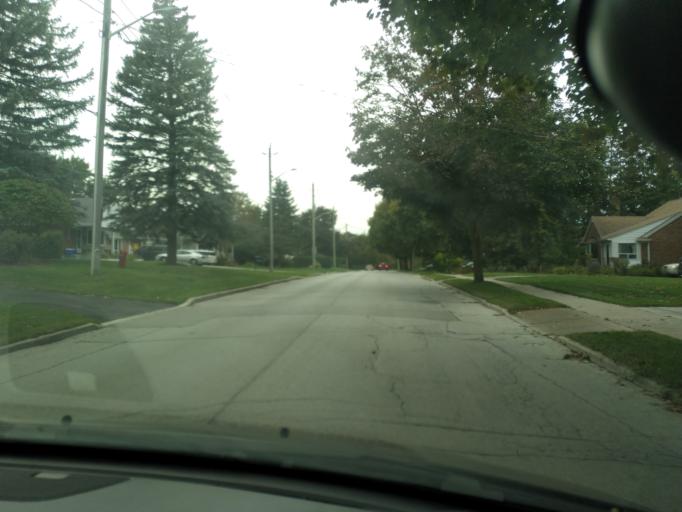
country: CA
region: Ontario
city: Newmarket
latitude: 44.0601
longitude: -79.4461
